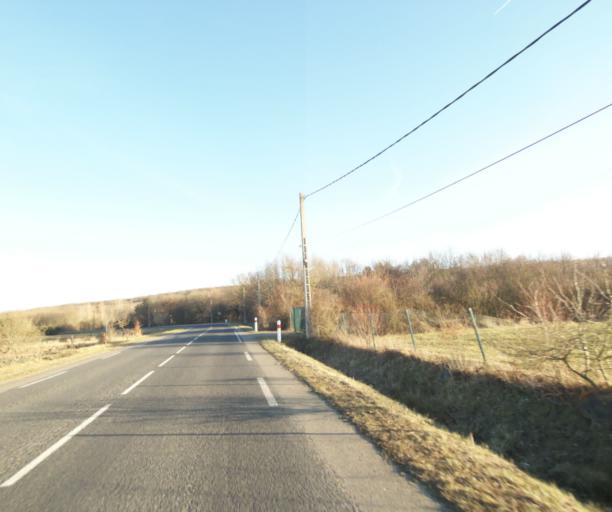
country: FR
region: Lorraine
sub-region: Departement de Meurthe-et-Moselle
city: Seichamps
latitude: 48.7034
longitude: 6.2713
